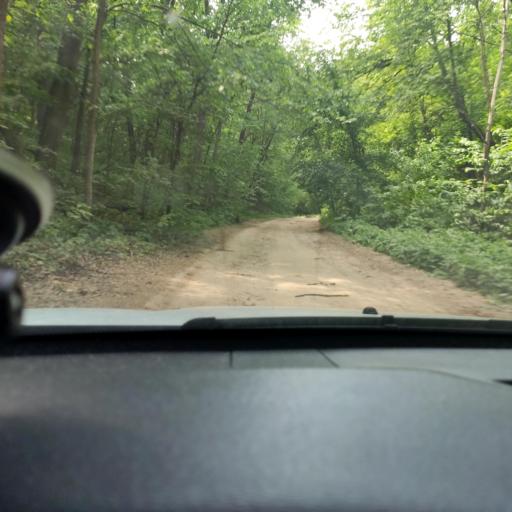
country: RU
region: Samara
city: Volzhskiy
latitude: 53.3380
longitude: 50.2200
